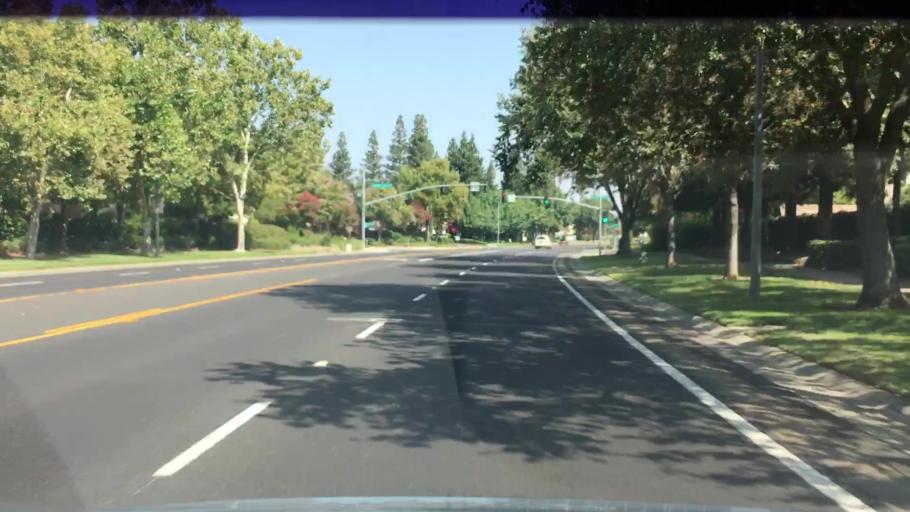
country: US
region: California
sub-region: Sacramento County
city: Laguna
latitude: 38.4138
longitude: -121.4067
